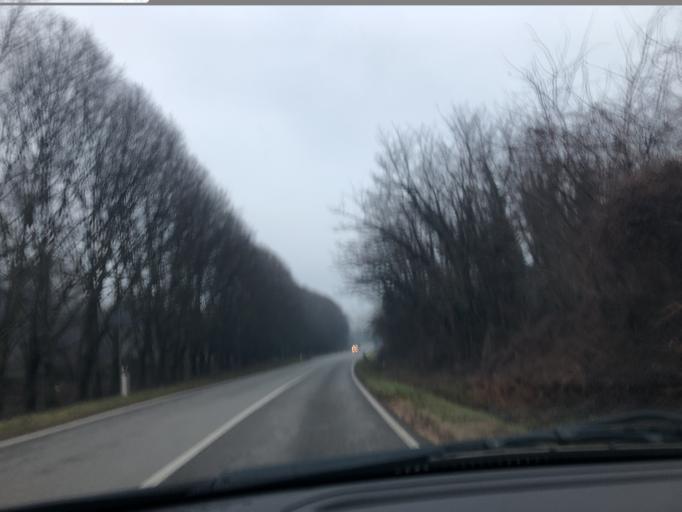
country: IT
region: Lombardy
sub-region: Provincia di Monza e Brianza
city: Aicurzio
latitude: 45.6333
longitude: 9.4132
